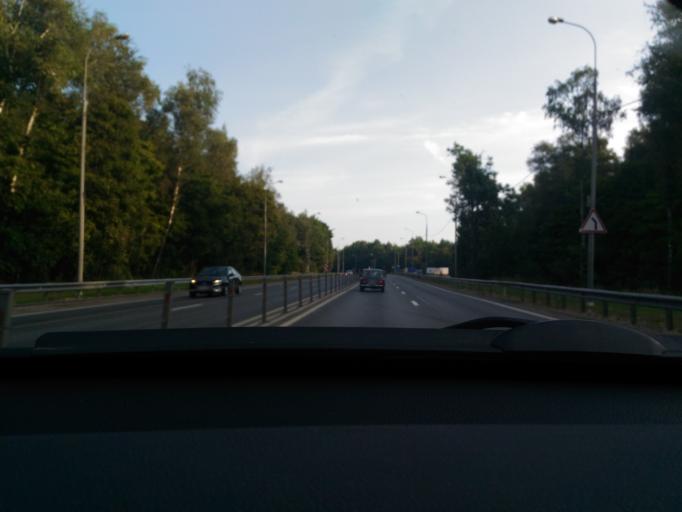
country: RU
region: Moskovskaya
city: Marfino
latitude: 56.0332
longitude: 37.5425
